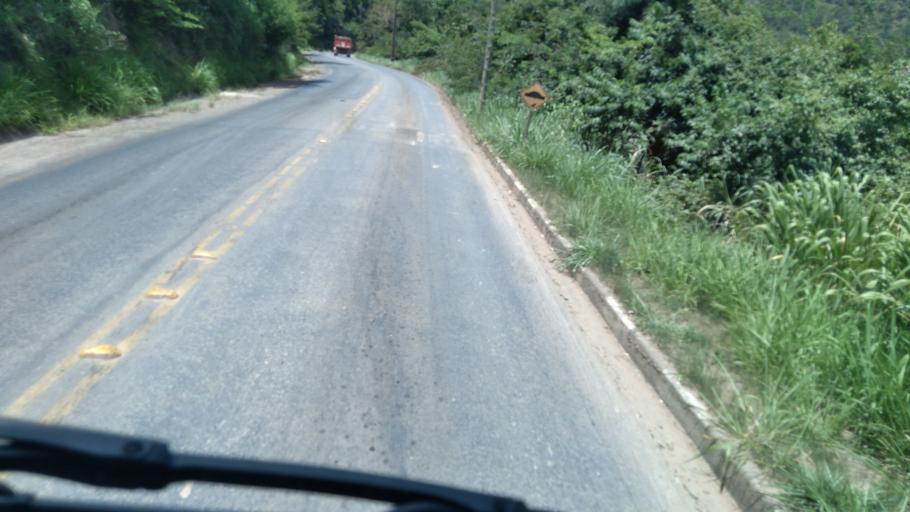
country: BR
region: Minas Gerais
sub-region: Santa Luzia
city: Santa Luzia
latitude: -19.8586
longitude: -43.8497
